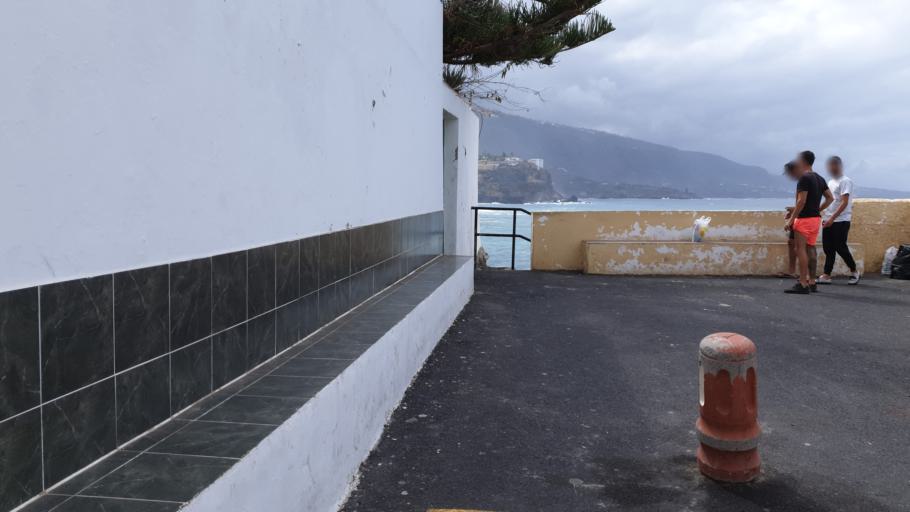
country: ES
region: Canary Islands
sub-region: Provincia de Santa Cruz de Tenerife
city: Puerto de la Cruz
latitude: 28.4116
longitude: -16.5662
